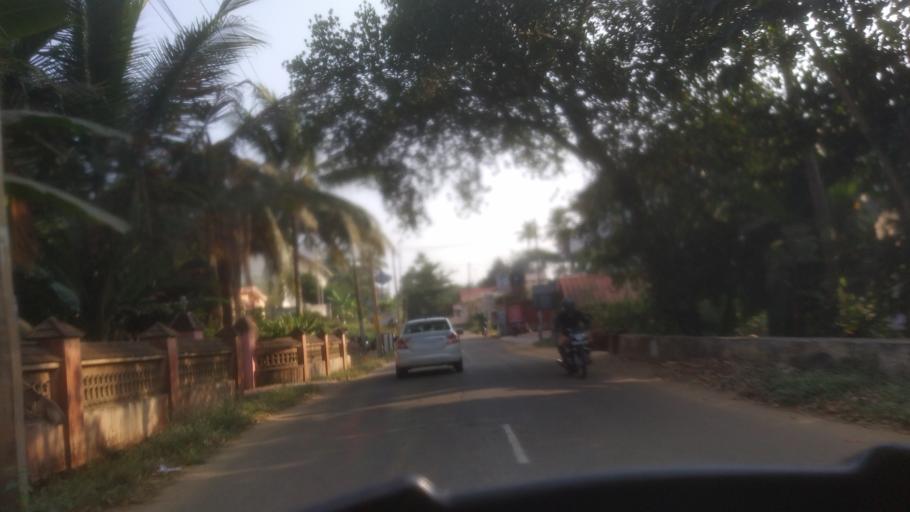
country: IN
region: Kerala
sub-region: Ernakulam
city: Piravam
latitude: 9.8237
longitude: 76.5021
